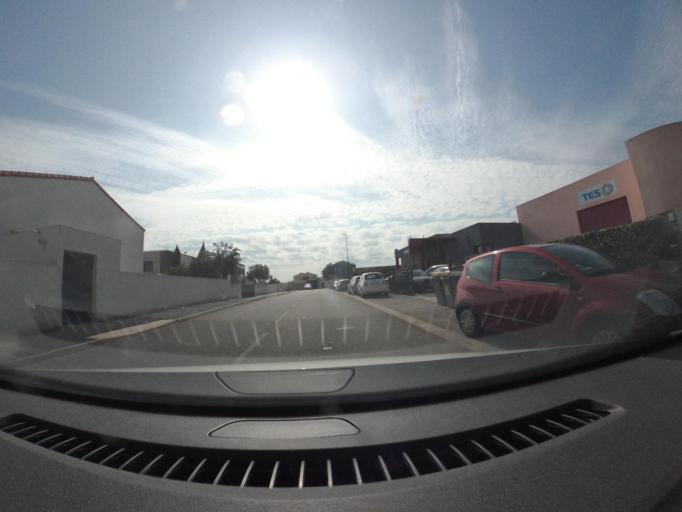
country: FR
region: Languedoc-Roussillon
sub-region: Departement de l'Herault
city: Baillargues
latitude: 43.6576
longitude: 3.9999
